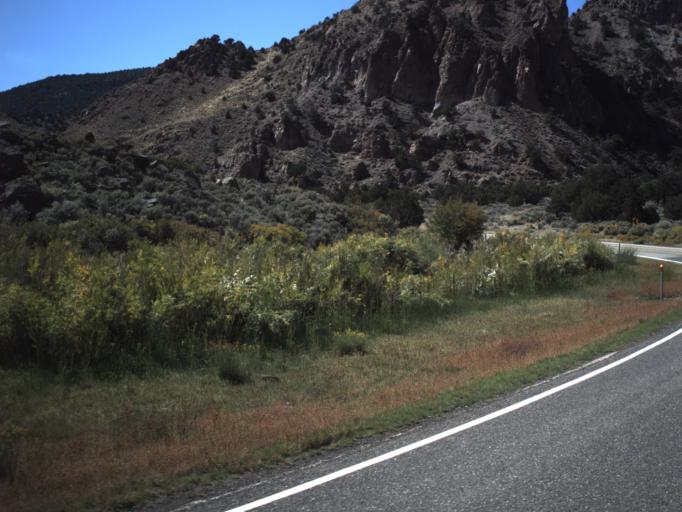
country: US
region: Utah
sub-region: Piute County
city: Junction
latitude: 38.1976
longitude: -112.1245
